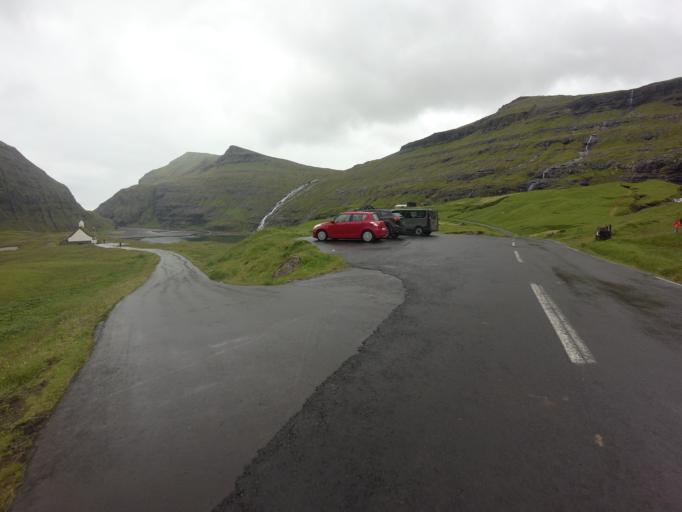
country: FO
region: Streymoy
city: Vestmanna
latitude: 62.2463
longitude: -7.1771
